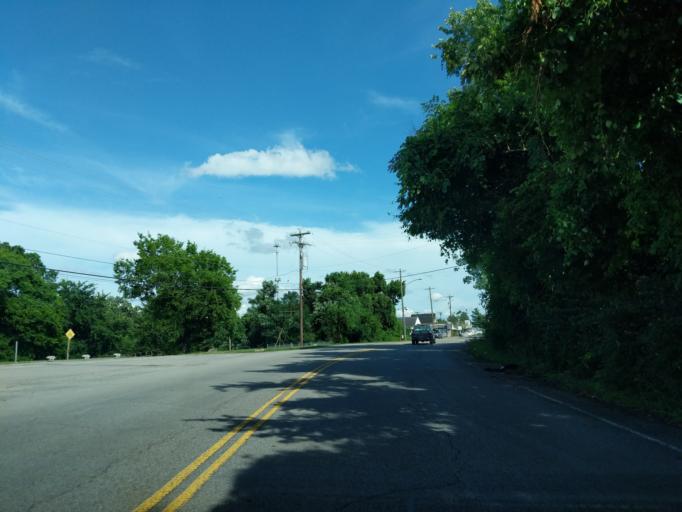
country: US
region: Tennessee
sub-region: Davidson County
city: Lakewood
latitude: 36.2663
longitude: -86.6521
